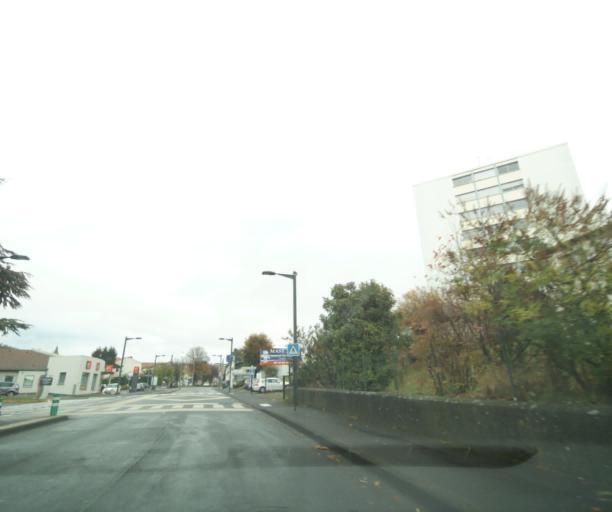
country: FR
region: Auvergne
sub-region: Departement du Puy-de-Dome
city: Cournon-d'Auvergne
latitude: 45.7375
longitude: 3.1948
